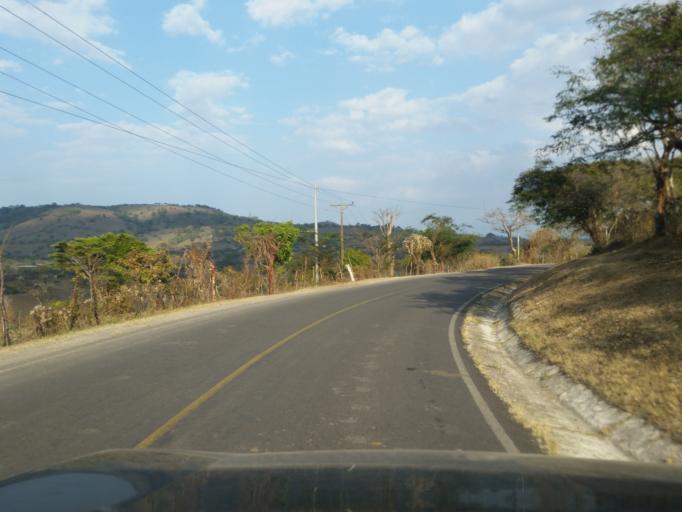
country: NI
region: Jinotega
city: San Rafael del Norte
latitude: 13.1951
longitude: -86.1239
